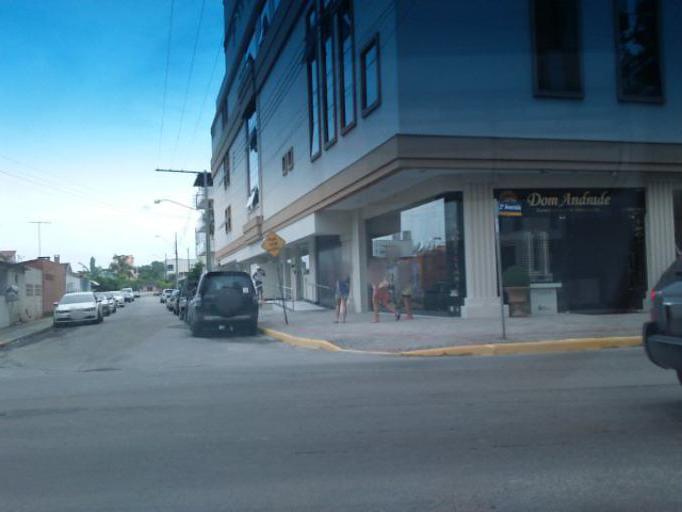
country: BR
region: Santa Catarina
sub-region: Itapema
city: Itapema
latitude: -27.1344
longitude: -48.6014
